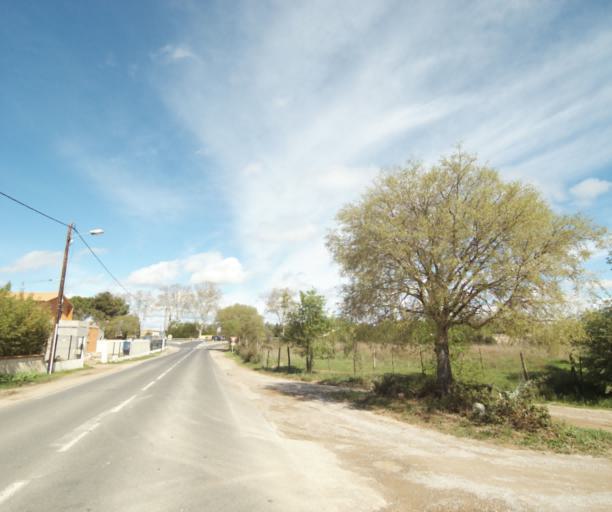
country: FR
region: Languedoc-Roussillon
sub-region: Departement de l'Herault
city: Villeneuve-les-Maguelone
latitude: 43.5537
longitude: 3.8455
